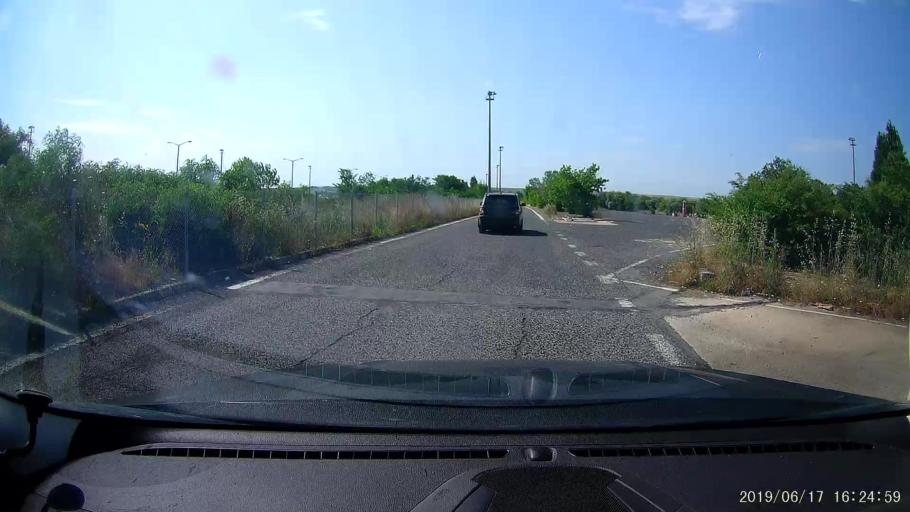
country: TR
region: Tekirdag
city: Marmaracik
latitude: 41.2893
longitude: 27.7842
